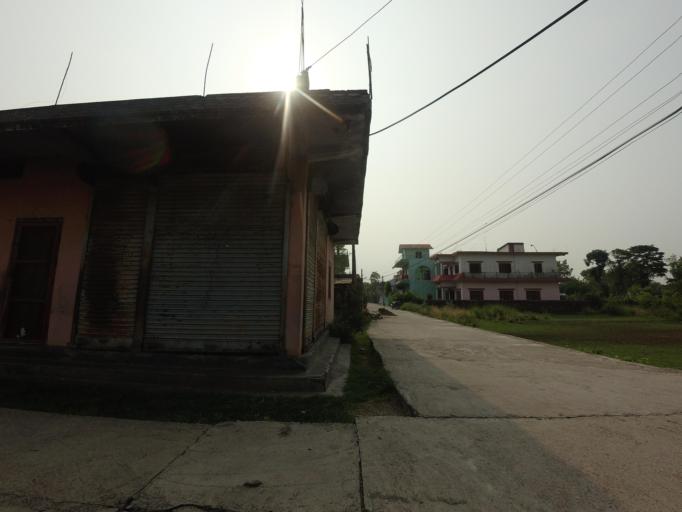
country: NP
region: Western Region
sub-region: Lumbini Zone
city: Bhairahawa
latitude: 27.5230
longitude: 83.4576
